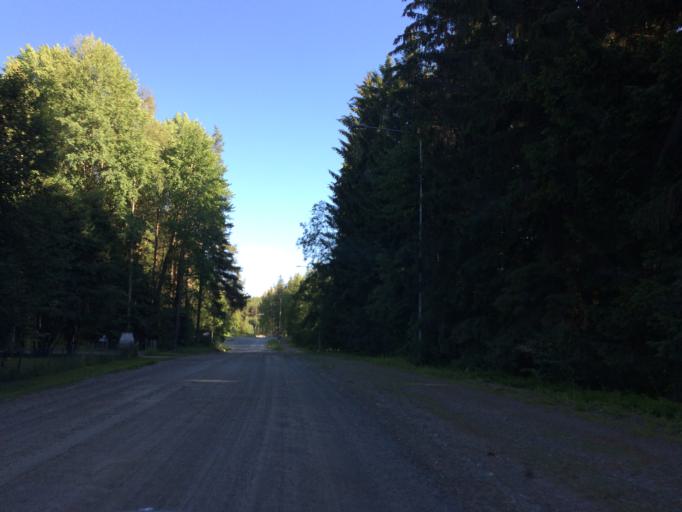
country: FI
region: Haeme
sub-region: Haemeenlinna
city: Haemeenlinna
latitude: 60.9876
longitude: 24.5062
